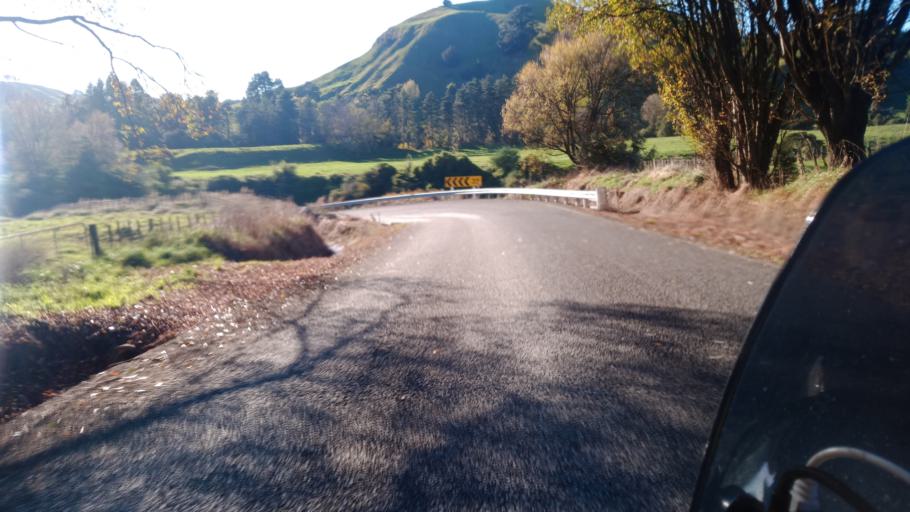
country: NZ
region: Hawke's Bay
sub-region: Wairoa District
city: Wairoa
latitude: -38.8711
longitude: 177.2121
